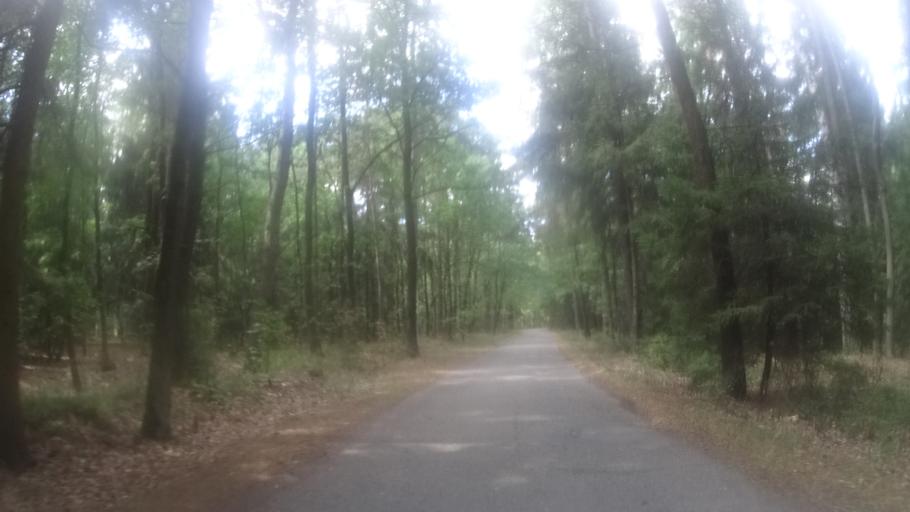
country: CZ
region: Pardubicky
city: Horni Jeleni
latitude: 50.0549
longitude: 16.1509
